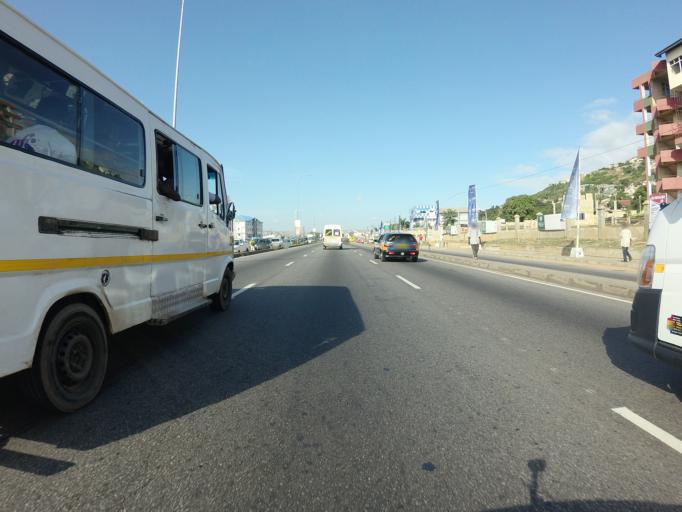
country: GH
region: Greater Accra
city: Gbawe
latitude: 5.5587
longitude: -0.2959
